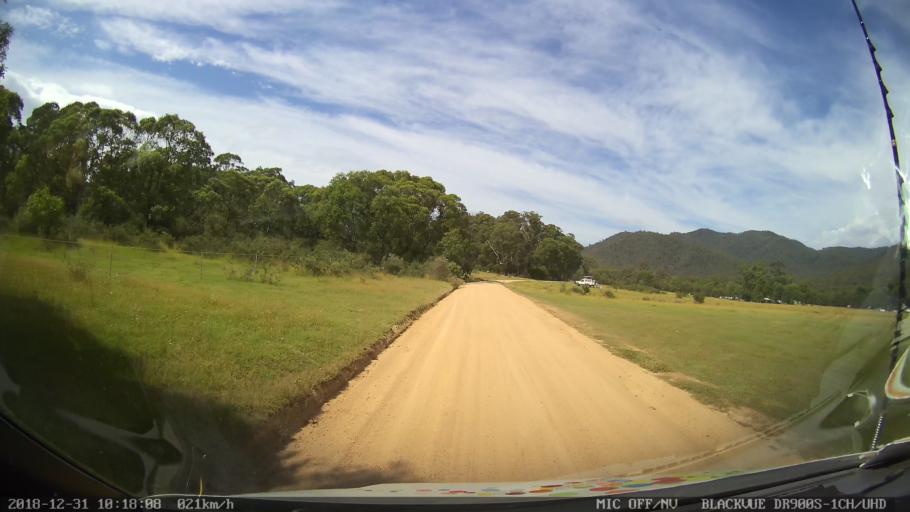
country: AU
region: New South Wales
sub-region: Snowy River
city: Jindabyne
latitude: -36.5424
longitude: 148.1339
